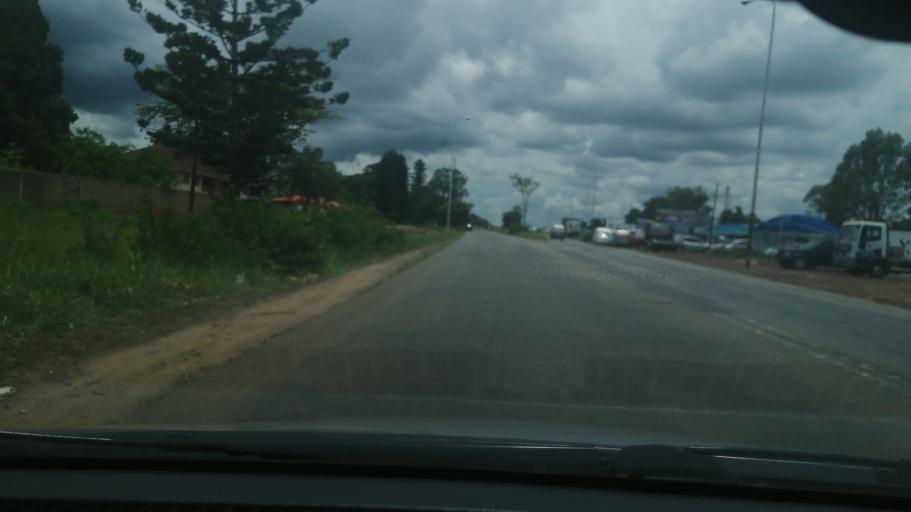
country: ZW
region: Harare
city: Harare
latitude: -17.8325
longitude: 31.0839
